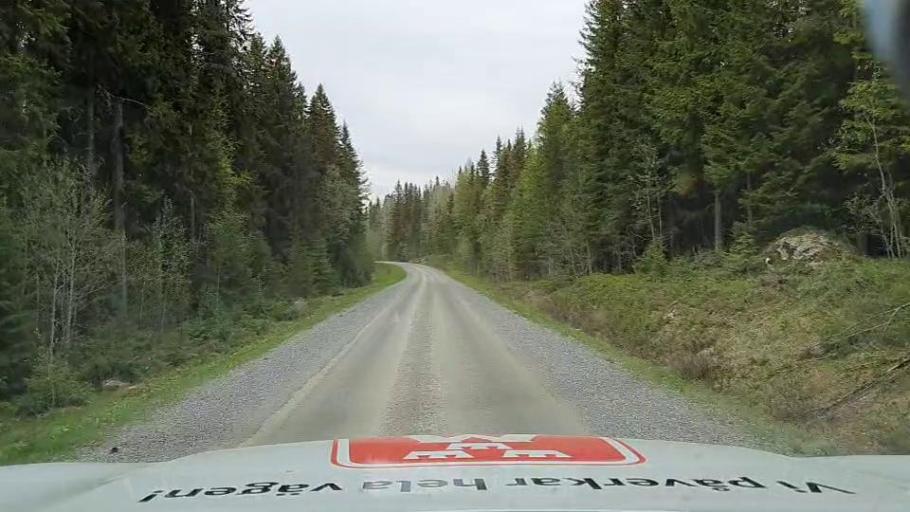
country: SE
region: Jaemtland
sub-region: OEstersunds Kommun
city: Brunflo
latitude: 62.6383
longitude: 14.9348
